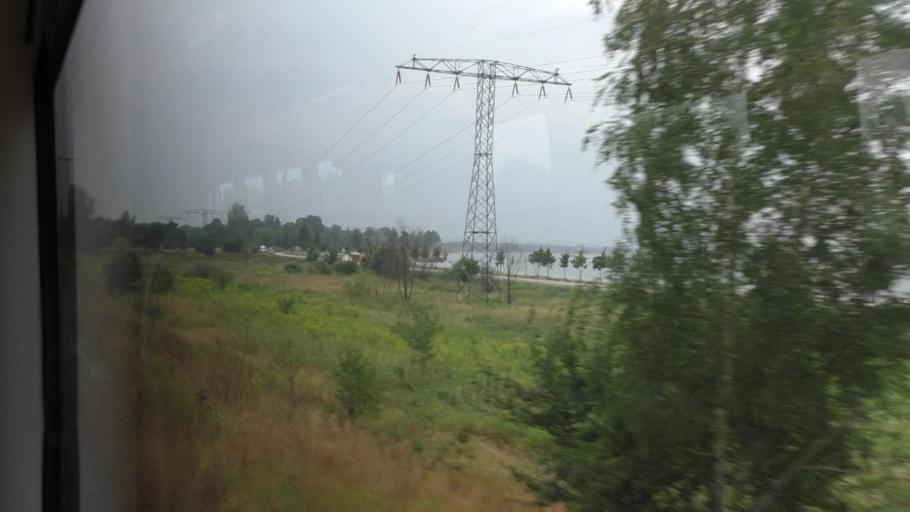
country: DE
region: Saxony
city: Goerlitz
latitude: 51.1061
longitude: 14.9773
